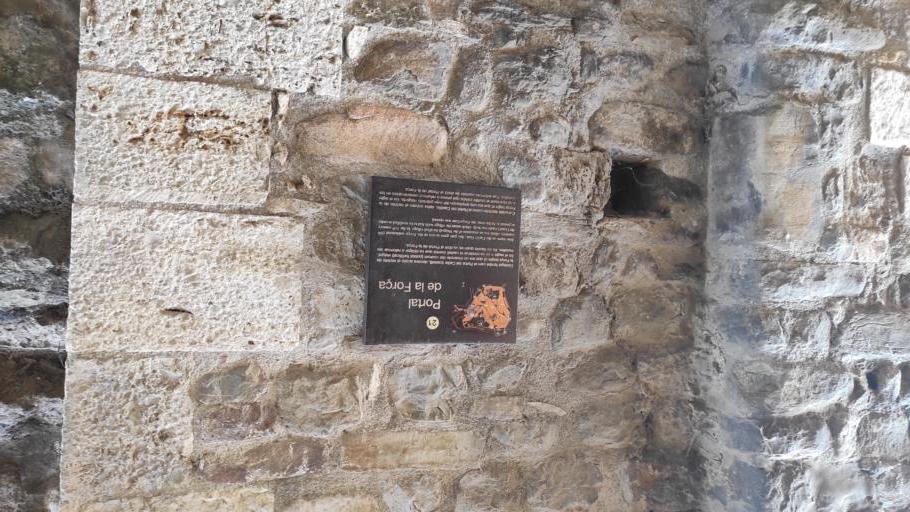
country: ES
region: Catalonia
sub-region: Provincia de Girona
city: Besalu
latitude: 42.1995
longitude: 2.7002
